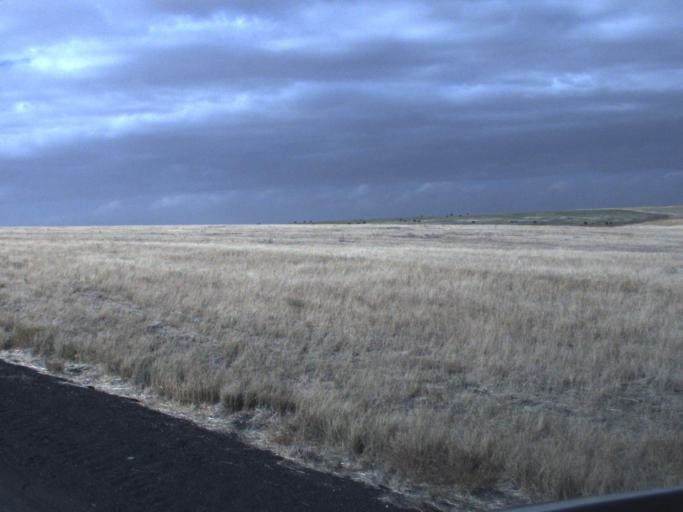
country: US
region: Washington
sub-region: Okanogan County
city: Coulee Dam
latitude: 47.6125
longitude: -118.7487
